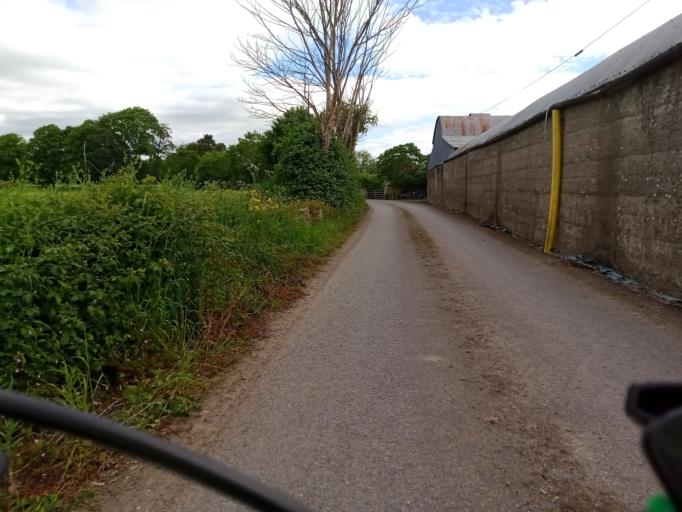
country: IE
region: Leinster
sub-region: Kilkenny
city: Kilkenny
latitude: 52.6497
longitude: -7.2139
